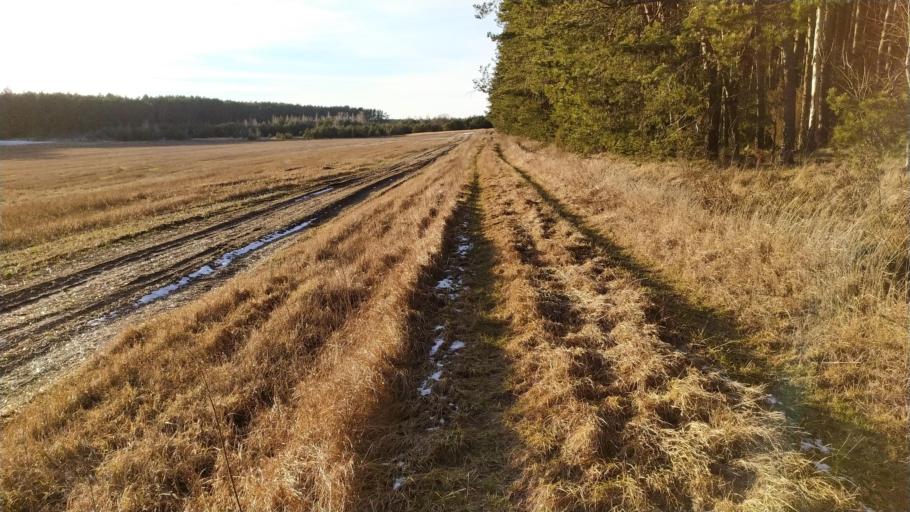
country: BY
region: Brest
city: Kamyanyets
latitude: 52.3708
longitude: 23.8520
